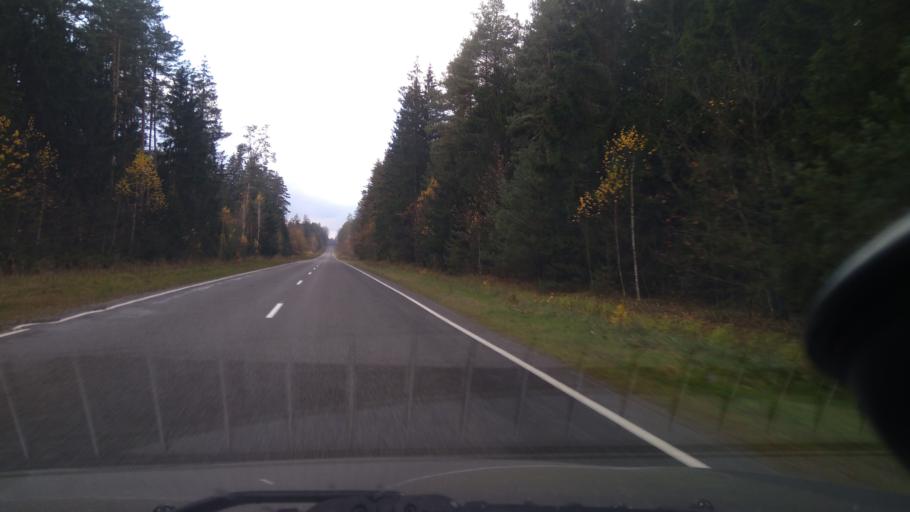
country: BY
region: Minsk
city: Urechcha
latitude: 53.2087
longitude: 27.9516
